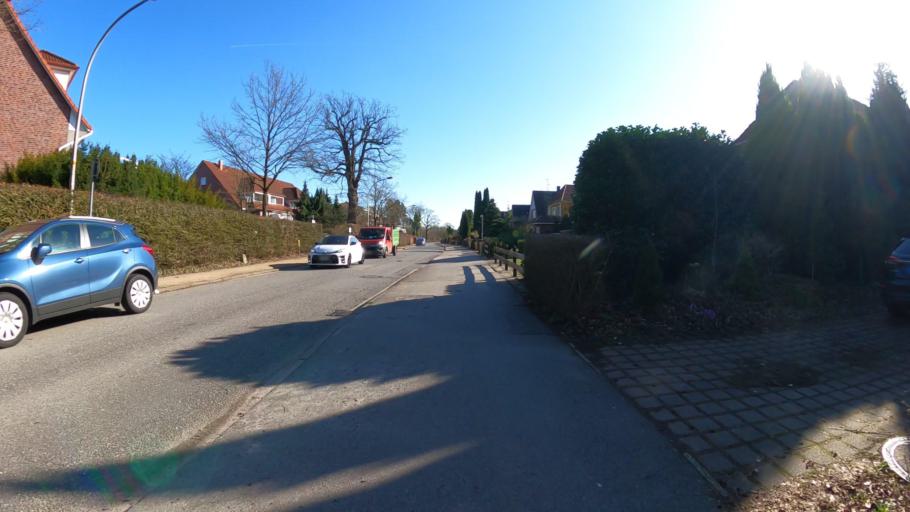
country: DE
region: Schleswig-Holstein
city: Rellingen
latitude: 53.6427
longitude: 9.7995
